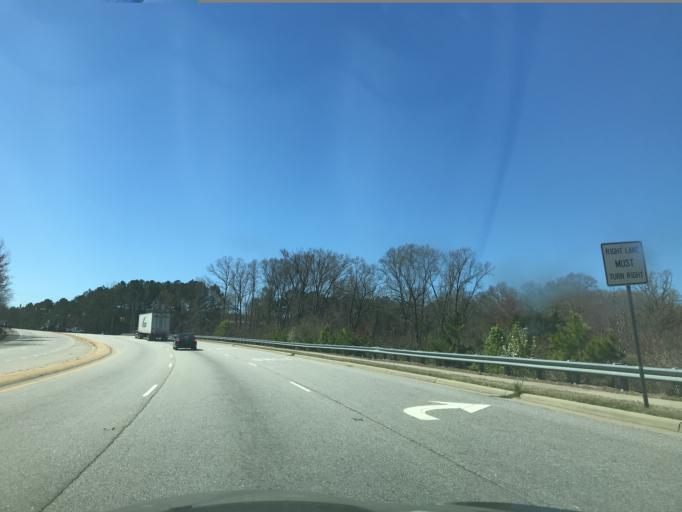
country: US
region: North Carolina
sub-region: Wake County
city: Raleigh
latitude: 35.7443
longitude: -78.6399
